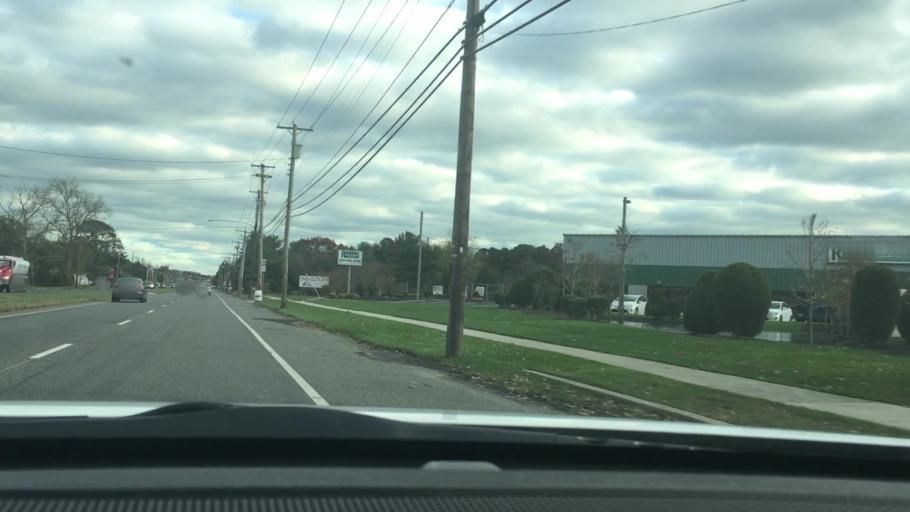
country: US
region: New Jersey
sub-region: Atlantic County
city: Northfield
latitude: 39.4129
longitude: -74.5732
